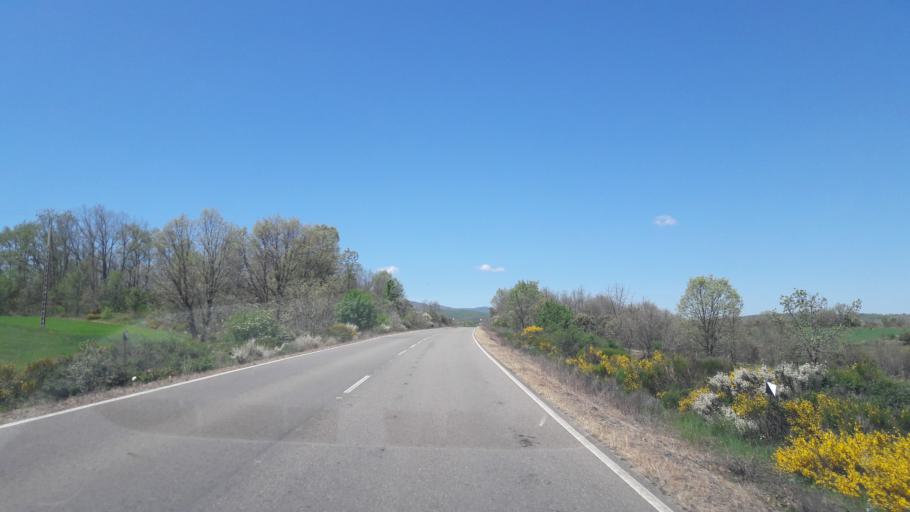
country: ES
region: Castille and Leon
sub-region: Provincia de Salamanca
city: Monleon
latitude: 40.5914
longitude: -5.8785
